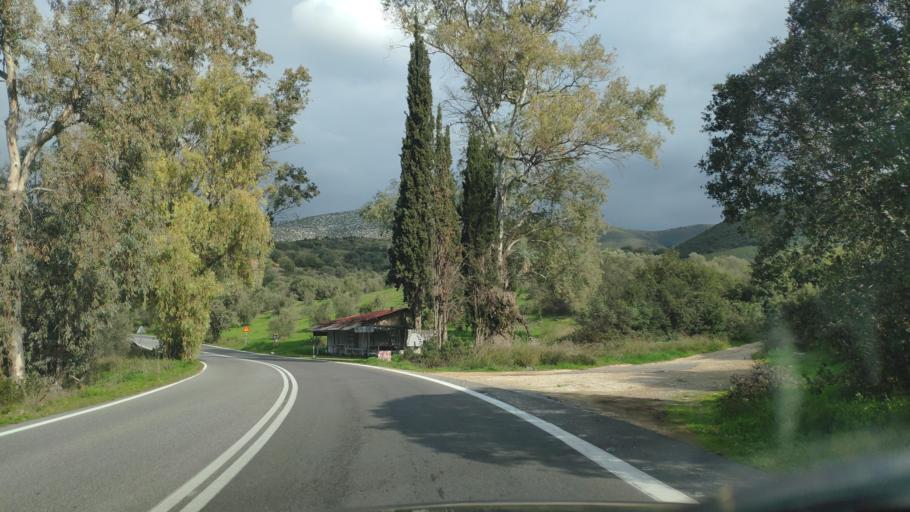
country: GR
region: Peloponnese
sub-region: Nomos Korinthias
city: Ayios Vasilios
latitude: 37.7724
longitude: 22.7254
